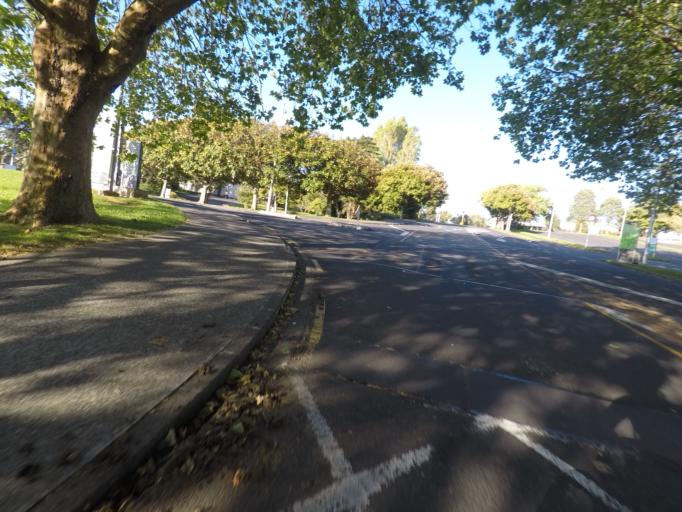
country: NZ
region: Auckland
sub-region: Auckland
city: Rosebank
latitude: -36.8806
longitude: 174.7102
